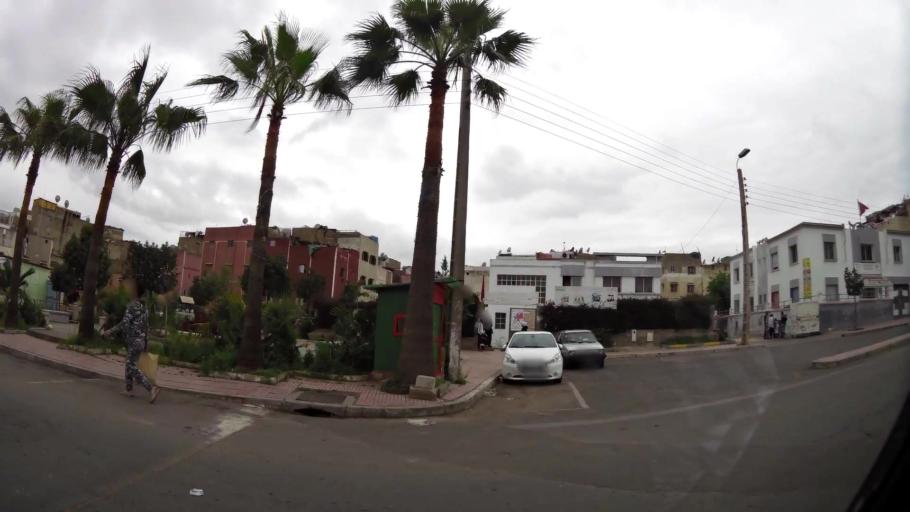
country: MA
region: Grand Casablanca
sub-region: Mediouna
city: Tit Mellil
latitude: 33.5639
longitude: -7.5408
